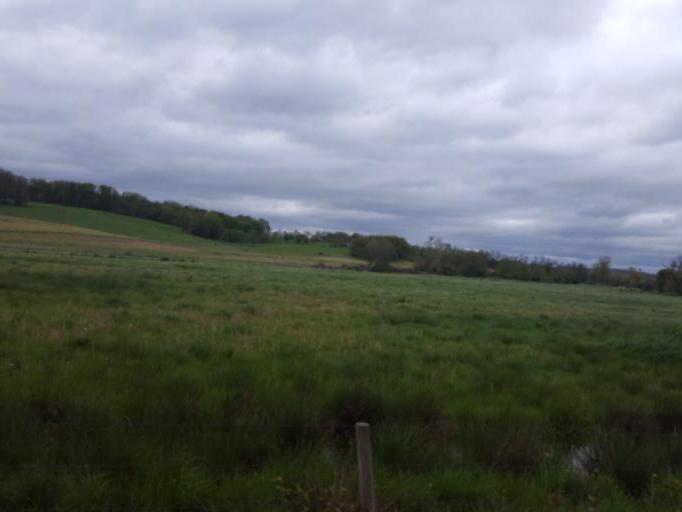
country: US
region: Ohio
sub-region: Knox County
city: Fredericktown
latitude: 40.5387
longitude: -82.4936
